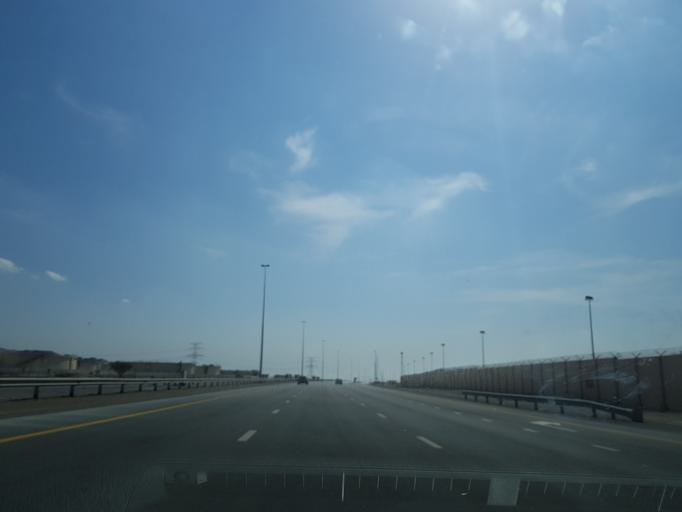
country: AE
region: Ra's al Khaymah
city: Ras al-Khaimah
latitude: 25.7770
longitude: 56.0298
